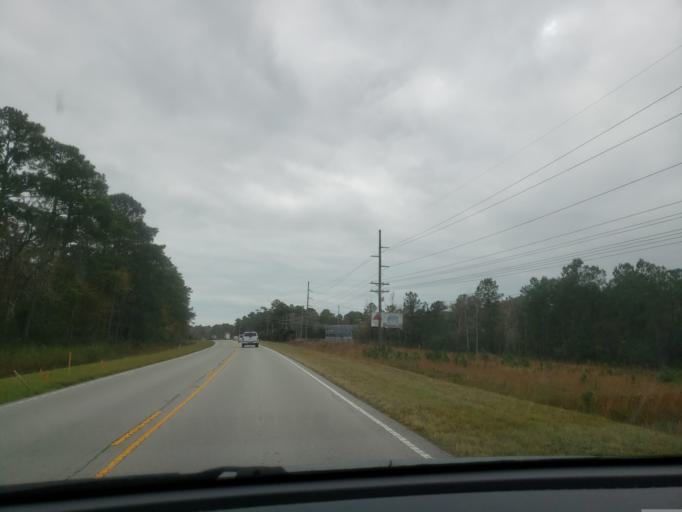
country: US
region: North Carolina
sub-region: Onslow County
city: Sneads Ferry
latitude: 34.5189
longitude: -77.4361
